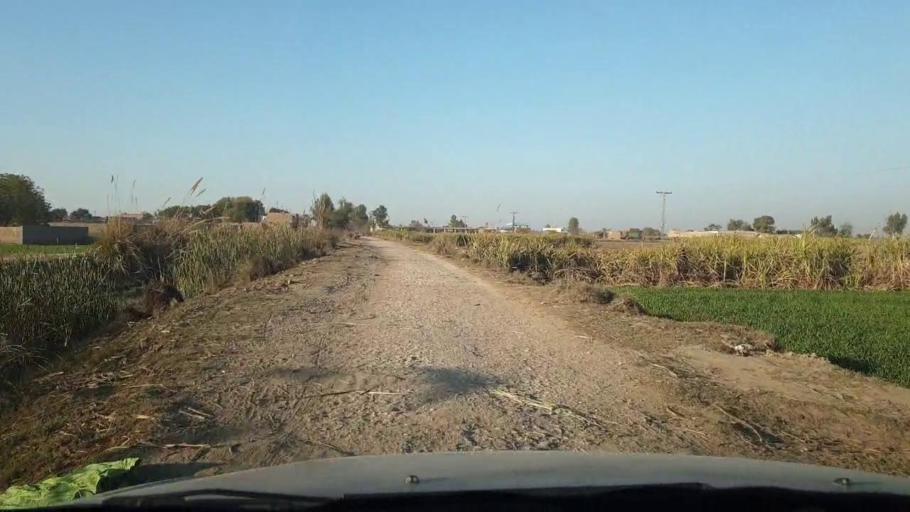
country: PK
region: Sindh
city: Ghotki
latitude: 27.9917
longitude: 69.2725
